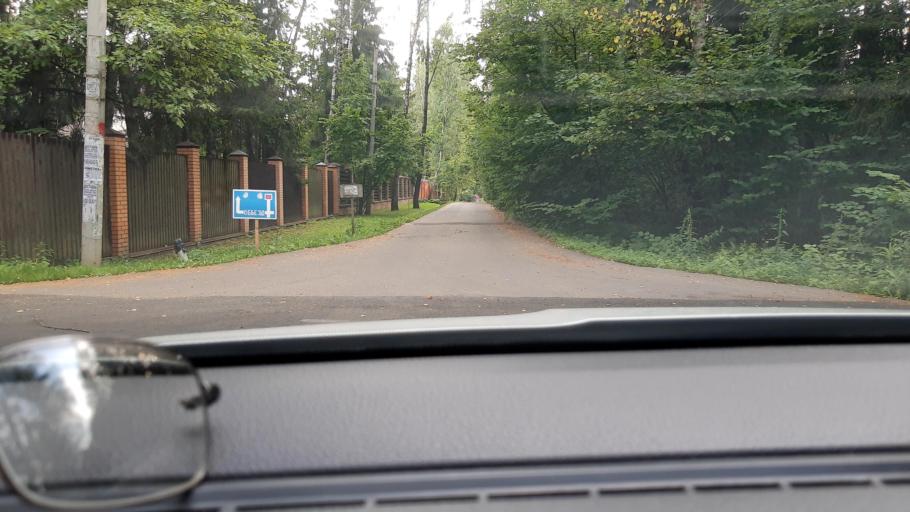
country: RU
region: Moskovskaya
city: Kokoshkino
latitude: 55.5924
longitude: 37.1644
